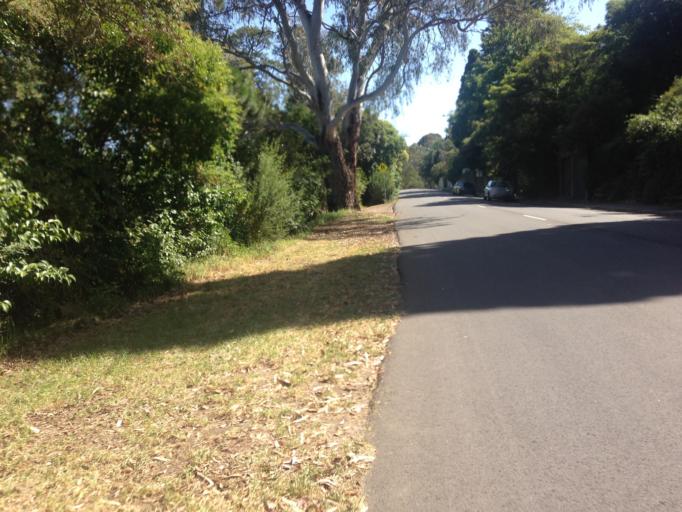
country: AU
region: Victoria
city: Ivanhoe East
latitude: -37.7769
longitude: 145.0458
